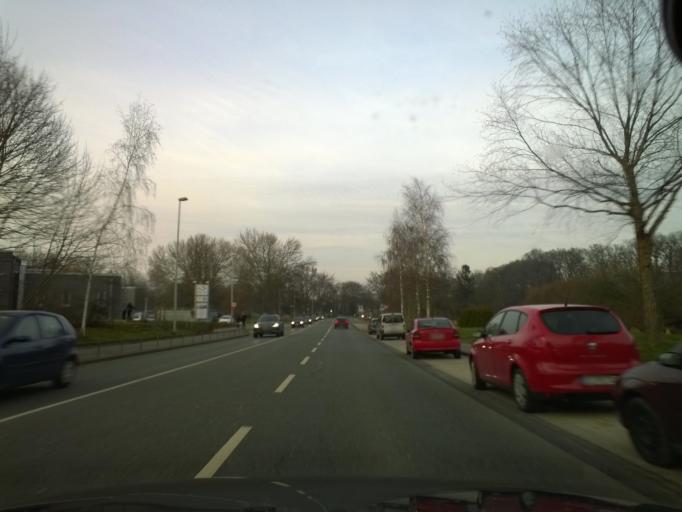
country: DE
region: Lower Saxony
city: Hildesheim
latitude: 52.1366
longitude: 9.9544
